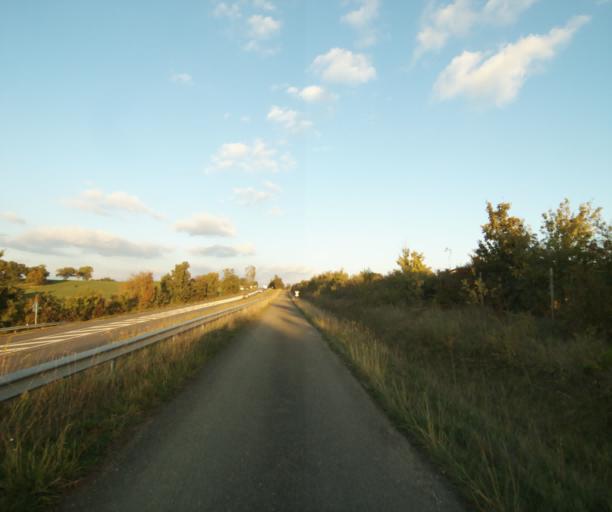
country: FR
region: Midi-Pyrenees
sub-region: Departement du Gers
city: Vic-Fezensac
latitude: 43.7593
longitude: 0.1932
